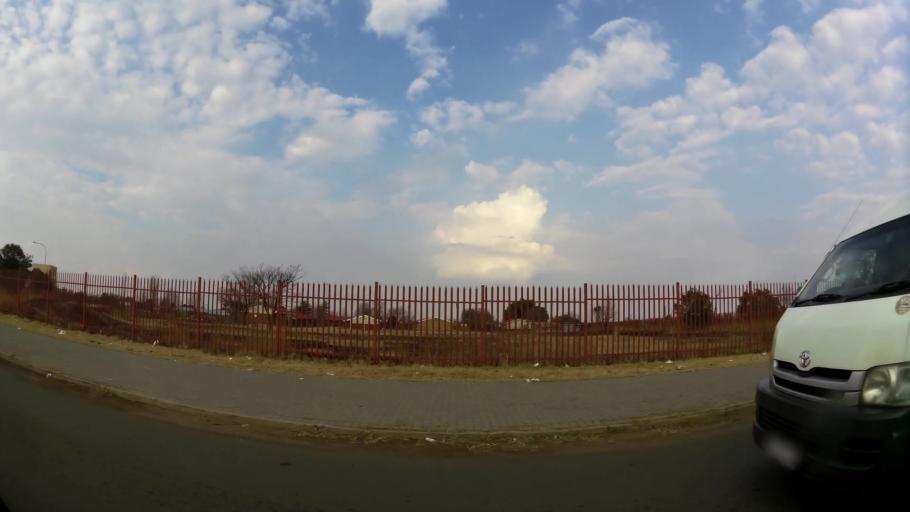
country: ZA
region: Gauteng
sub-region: Sedibeng District Municipality
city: Vanderbijlpark
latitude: -26.6888
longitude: 27.8678
